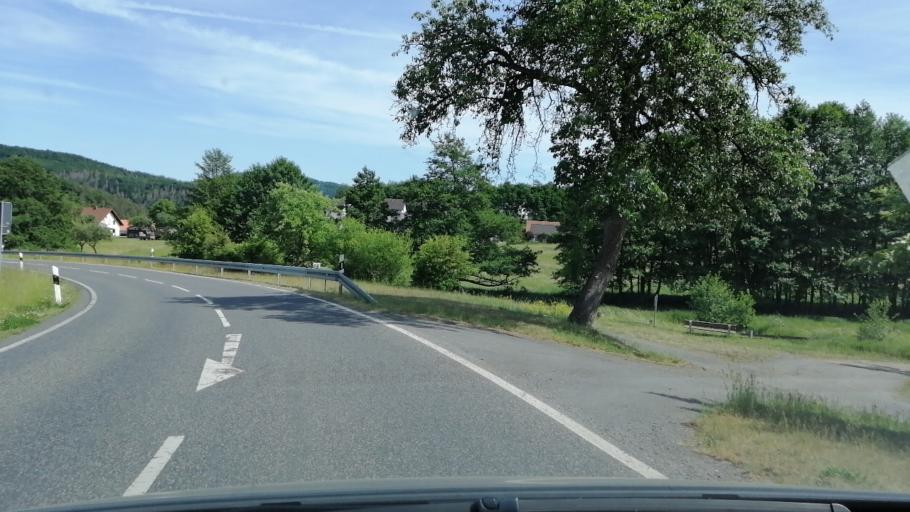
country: DE
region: Hesse
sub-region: Regierungsbezirk Kassel
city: Waldeck
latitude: 51.1747
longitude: 9.0423
